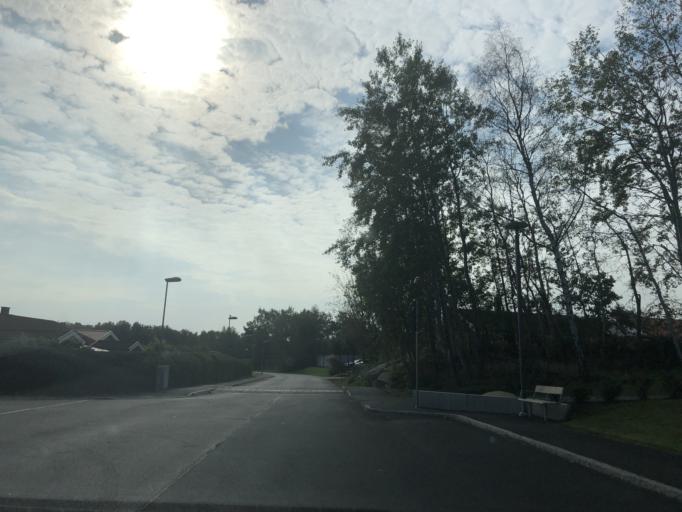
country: SE
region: Vaestra Goetaland
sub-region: Goteborg
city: Majorna
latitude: 57.6511
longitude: 11.8758
